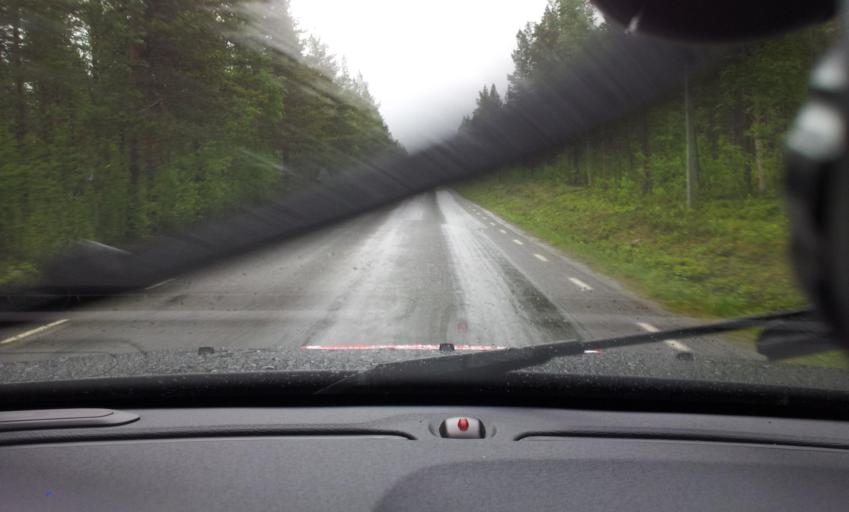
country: SE
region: Jaemtland
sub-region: Are Kommun
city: Are
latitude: 63.1697
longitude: 13.0807
